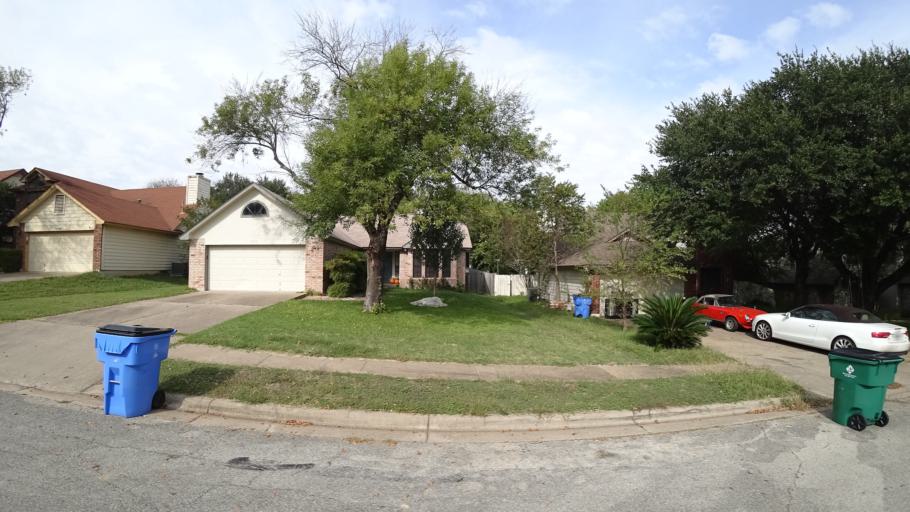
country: US
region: Texas
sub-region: Travis County
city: Wells Branch
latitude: 30.4402
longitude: -97.6820
